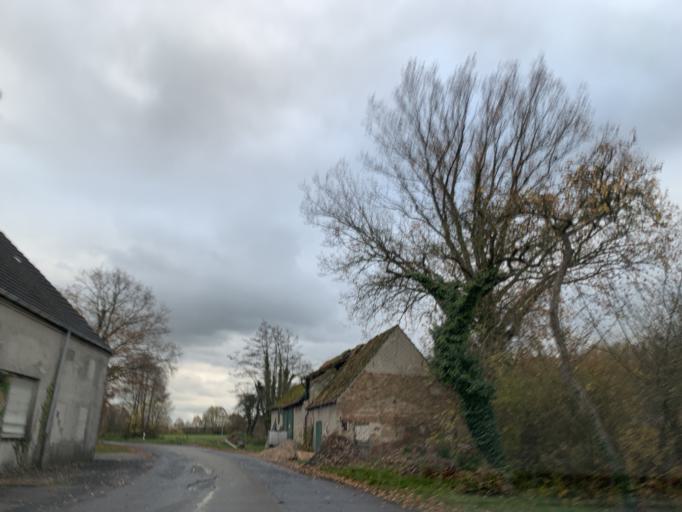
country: DE
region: North Rhine-Westphalia
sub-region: Regierungsbezirk Munster
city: Steinfurt
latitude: 52.1126
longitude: 7.3835
